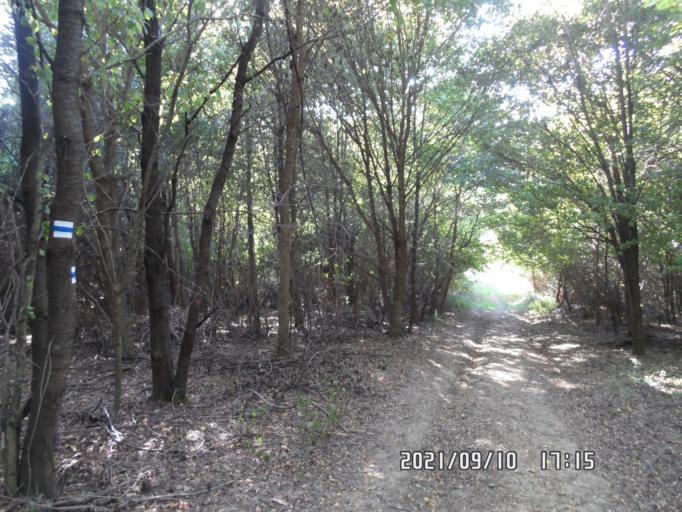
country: HU
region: Zala
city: Nagykanizsa
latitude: 46.5688
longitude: 17.0465
